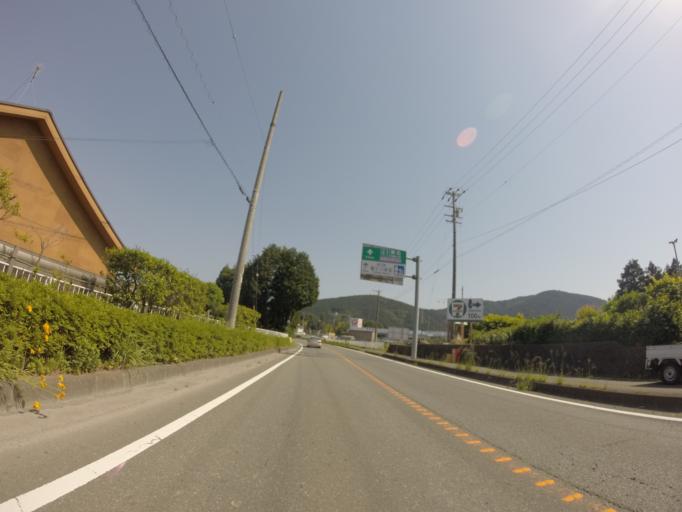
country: JP
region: Shizuoka
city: Fujinomiya
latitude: 35.1909
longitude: 138.5904
